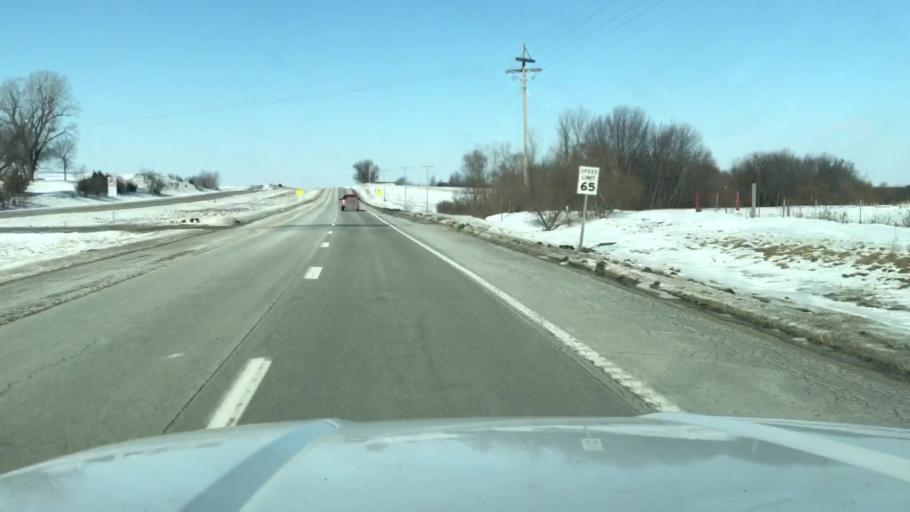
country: US
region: Missouri
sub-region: Andrew County
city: Savannah
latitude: 39.9662
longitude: -94.8660
